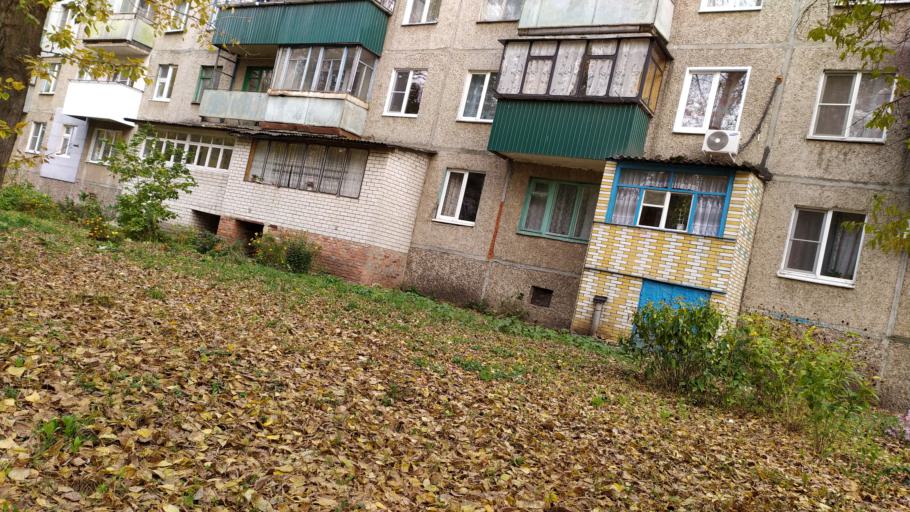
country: RU
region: Kursk
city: Kursk
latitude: 51.6508
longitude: 36.1399
